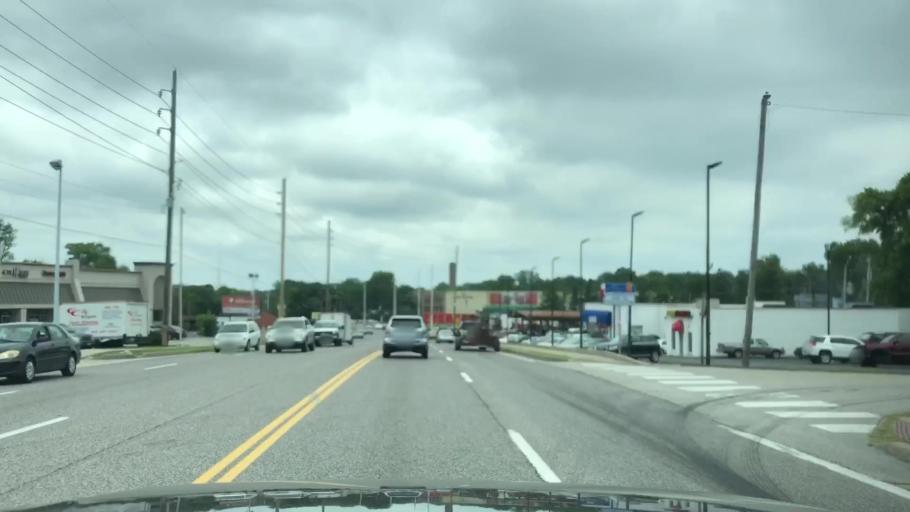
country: US
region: Missouri
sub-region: Saint Louis County
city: Florissant
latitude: 38.7985
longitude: -90.3246
